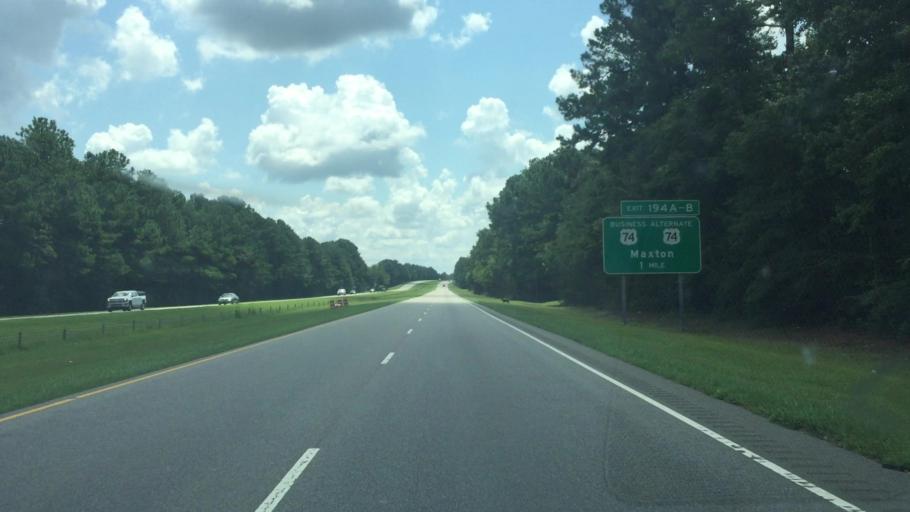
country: US
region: North Carolina
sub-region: Robeson County
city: Maxton
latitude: 34.7336
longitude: -79.3236
